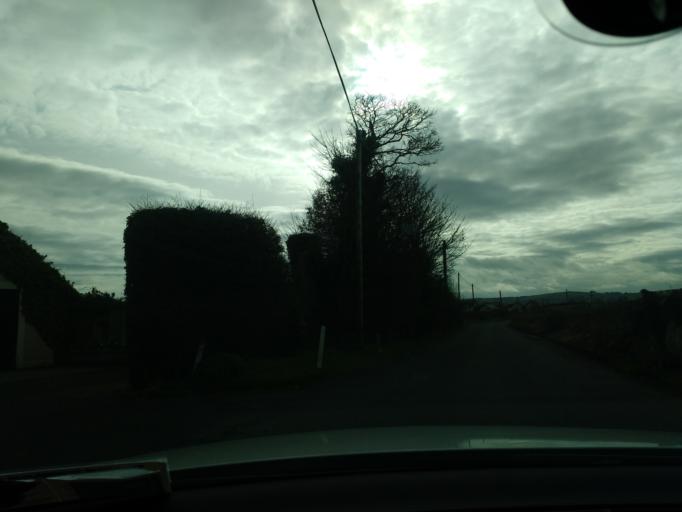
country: IE
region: Leinster
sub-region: Laois
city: Rathdowney
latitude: 52.6863
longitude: -7.6152
